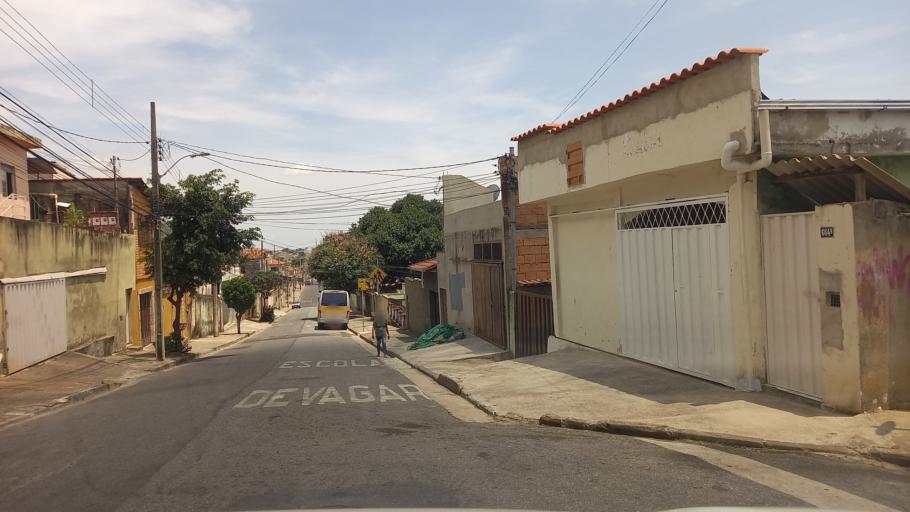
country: BR
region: Minas Gerais
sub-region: Contagem
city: Contagem
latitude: -19.9072
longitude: -44.0092
